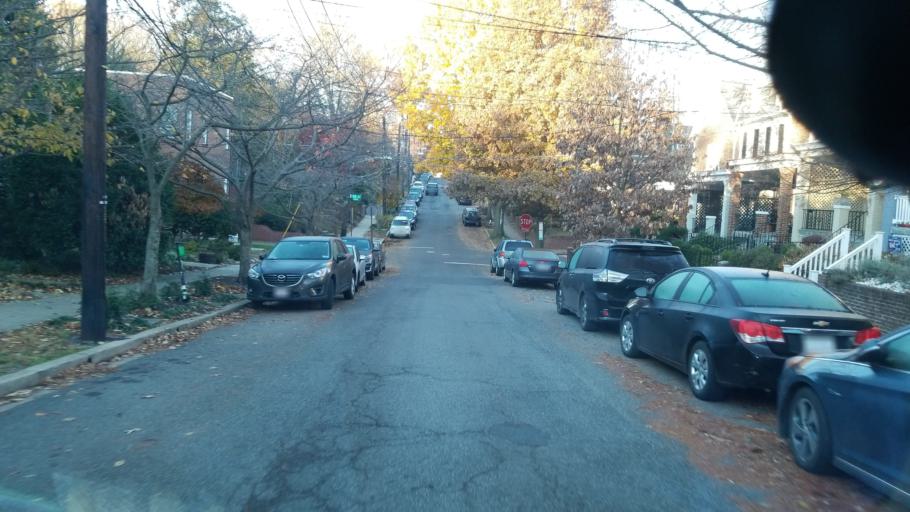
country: US
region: Maryland
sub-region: Montgomery County
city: Friendship Village
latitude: 38.9196
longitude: -77.0769
